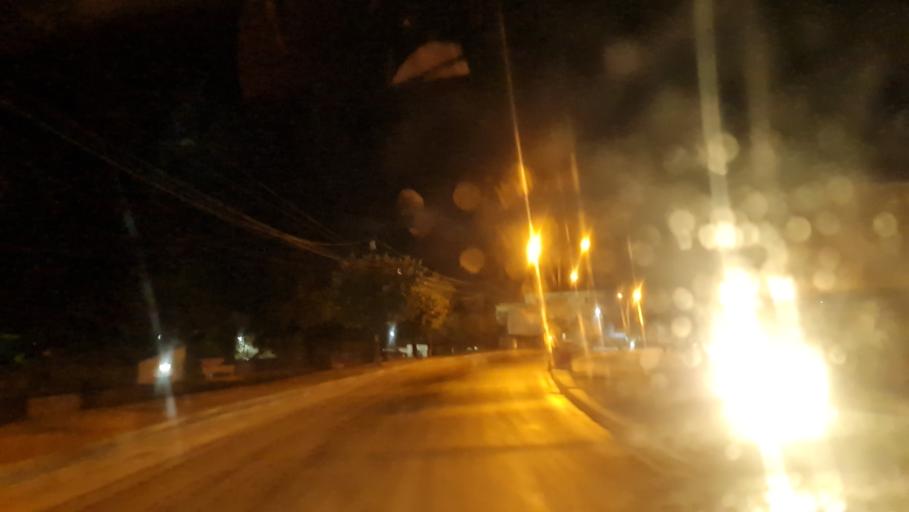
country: MZ
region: Nampula
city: Nampula
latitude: -15.1146
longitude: 39.2818
